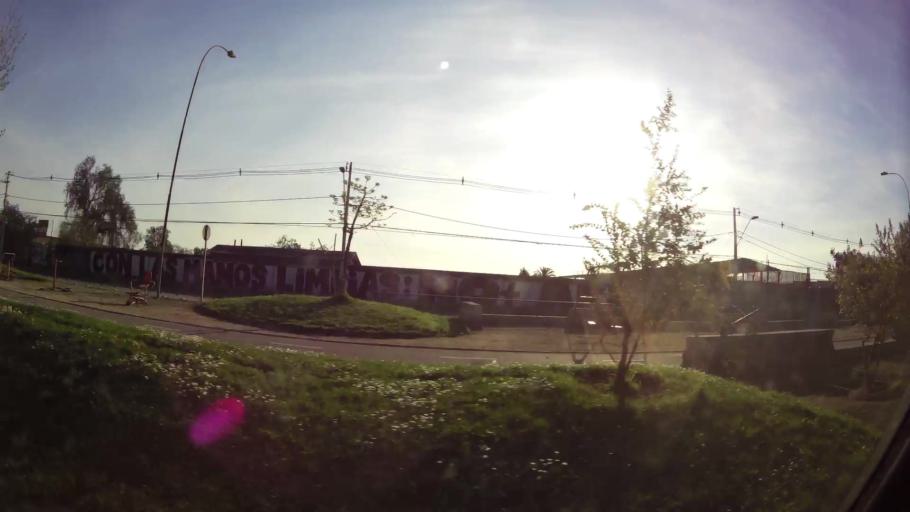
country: CL
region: Santiago Metropolitan
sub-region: Provincia de Santiago
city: Santiago
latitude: -33.4984
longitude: -70.6279
